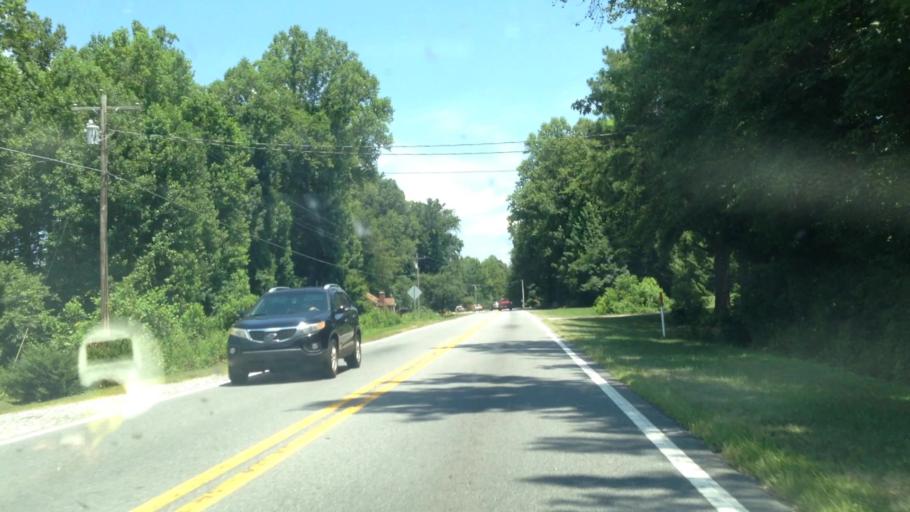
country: US
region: North Carolina
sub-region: Guilford County
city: Stokesdale
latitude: 36.2321
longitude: -80.0172
